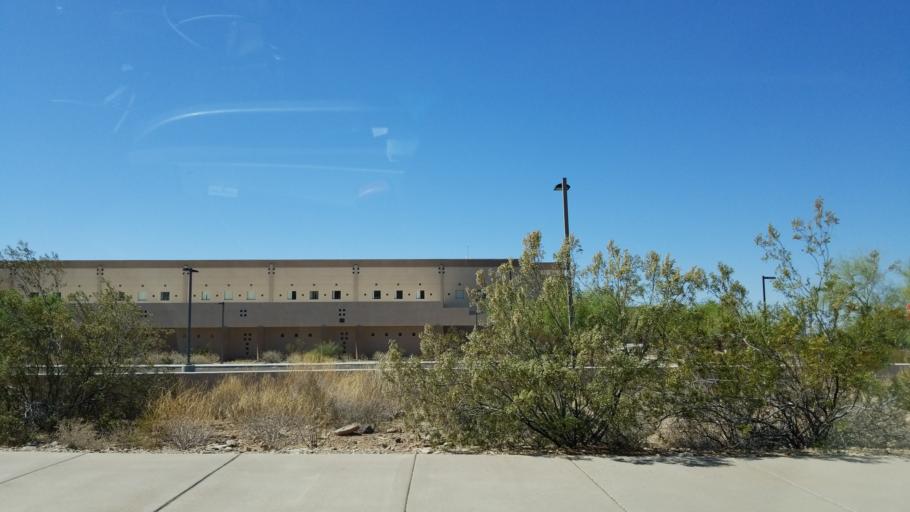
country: US
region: Arizona
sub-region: Maricopa County
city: Fountain Hills
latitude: 33.5896
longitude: -111.8113
